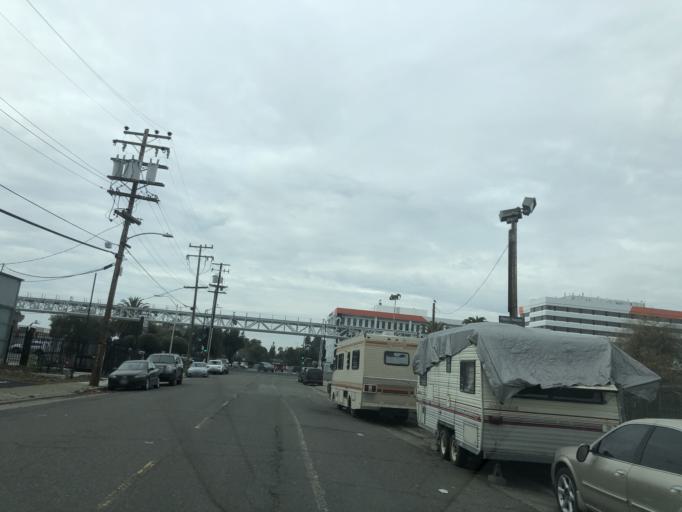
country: US
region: California
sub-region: Alameda County
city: San Leandro
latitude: 37.7341
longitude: -122.1967
